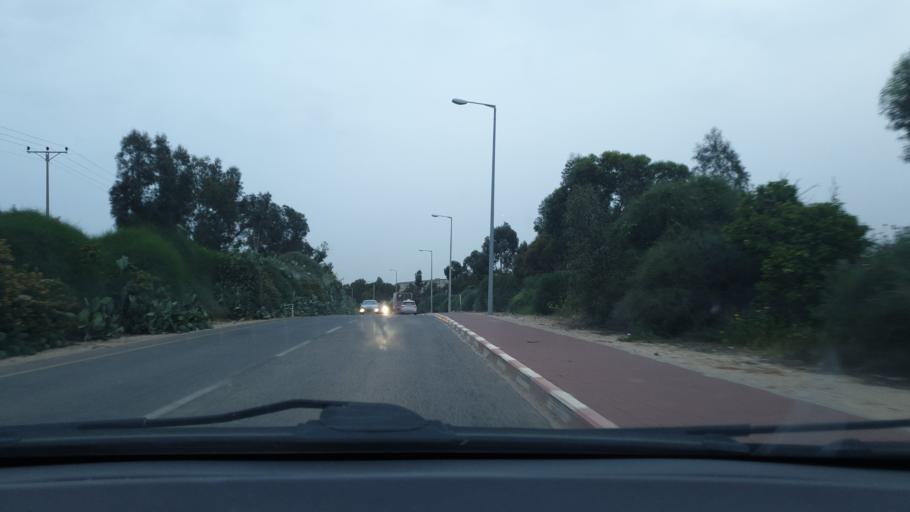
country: IL
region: Central District
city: Kefar Habad
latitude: 31.9834
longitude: 34.8413
